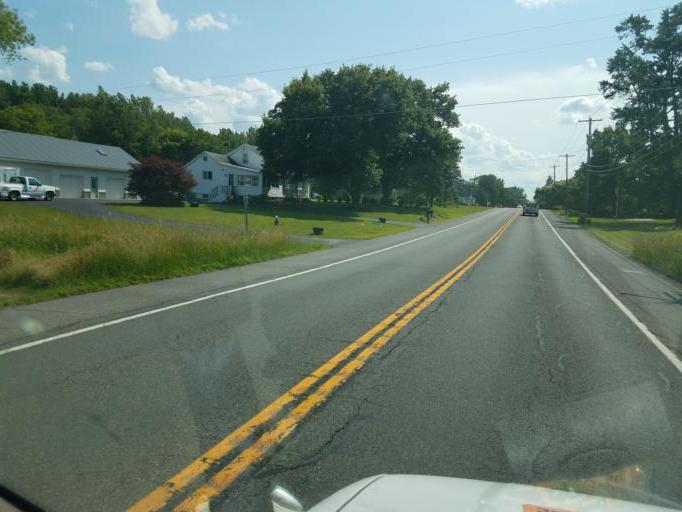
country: US
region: New York
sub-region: Ontario County
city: Geneva
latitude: 42.8889
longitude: -76.9262
